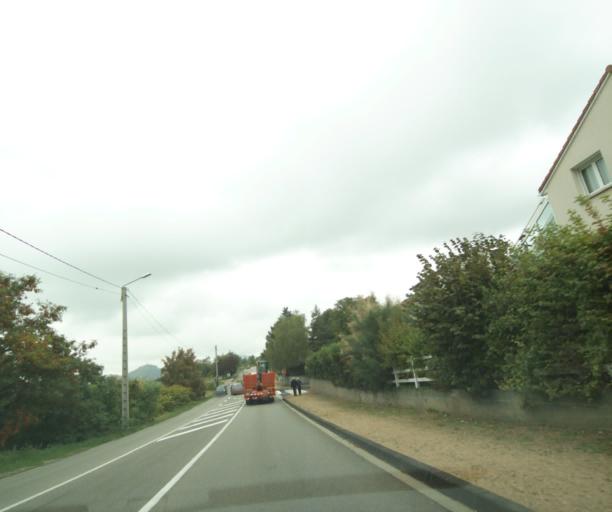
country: FR
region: Auvergne
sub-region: Departement du Puy-de-Dome
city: Royat
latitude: 45.7571
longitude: 3.0639
